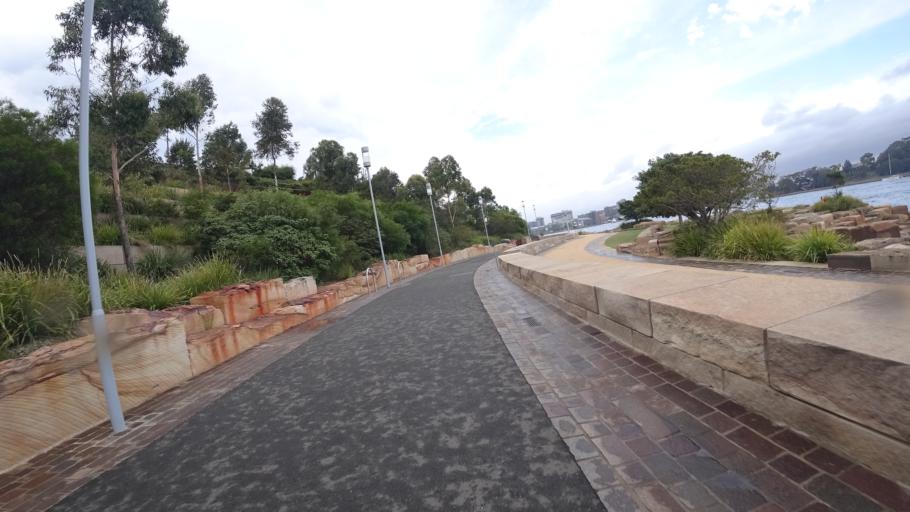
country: AU
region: New South Wales
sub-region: Leichhardt
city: Balmain East
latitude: -33.8571
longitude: 151.2006
